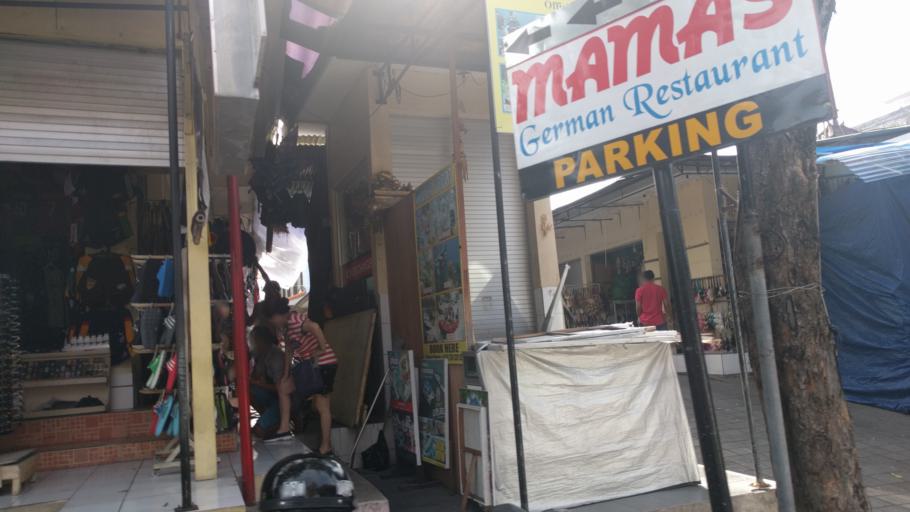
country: ID
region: Bali
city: Kuta
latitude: -8.7115
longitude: 115.1728
